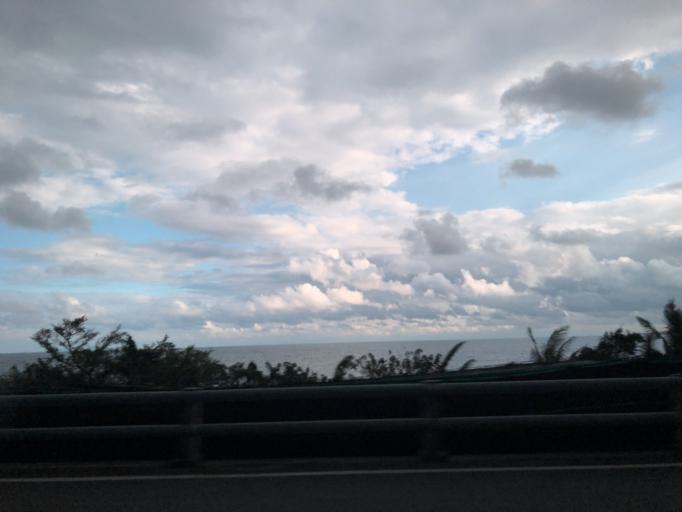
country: TW
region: Taiwan
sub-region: Taitung
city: Taitung
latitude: 22.8556
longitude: 121.1969
